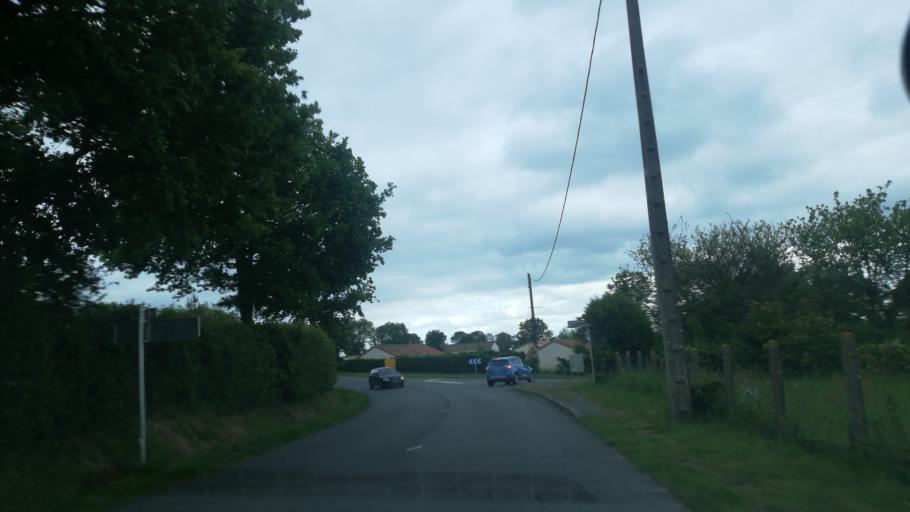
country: FR
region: Poitou-Charentes
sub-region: Departement des Deux-Sevres
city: La Chapelle-Saint-Laurent
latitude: 46.7648
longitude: -0.5192
